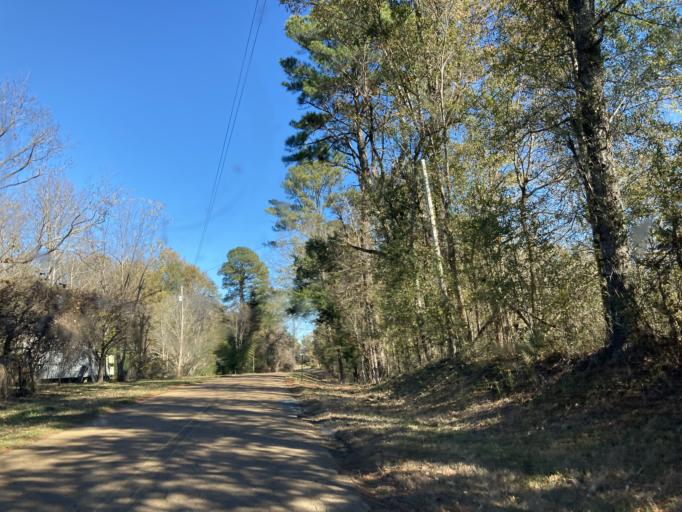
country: US
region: Mississippi
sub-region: Hinds County
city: Lynchburg
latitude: 32.5826
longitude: -90.5618
